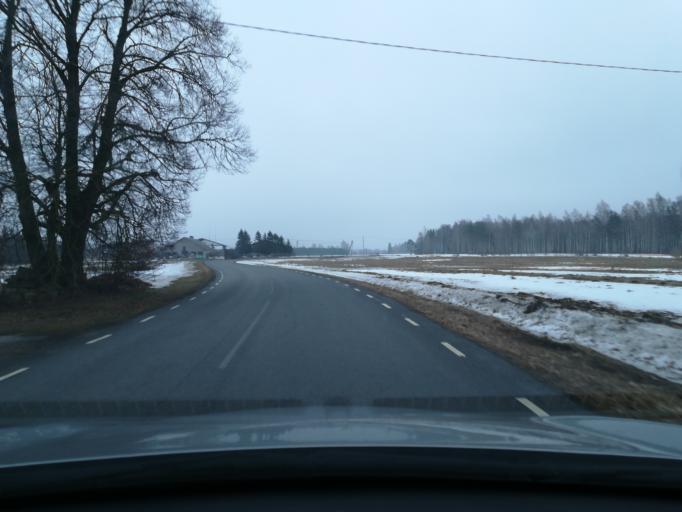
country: EE
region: Harju
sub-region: Kuusalu vald
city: Kuusalu
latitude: 59.4712
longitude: 25.5323
